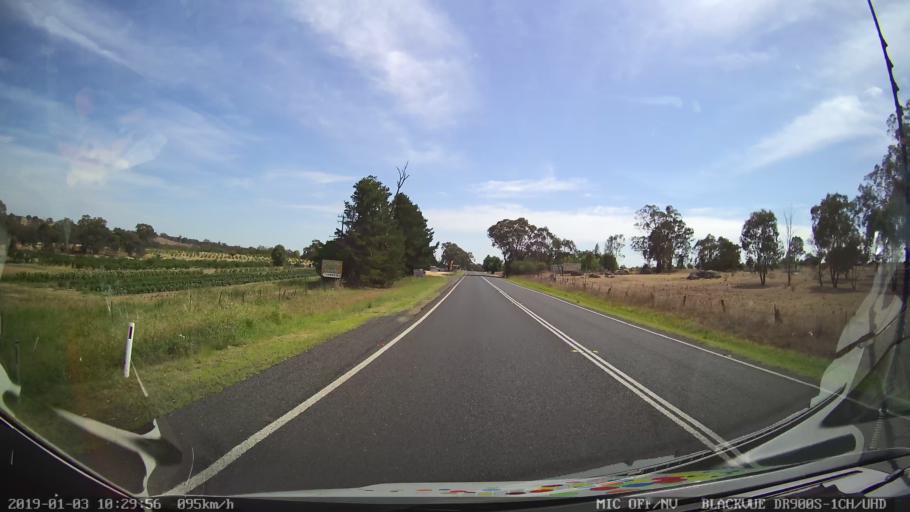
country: AU
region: New South Wales
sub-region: Young
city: Young
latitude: -34.3677
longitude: 148.2629
